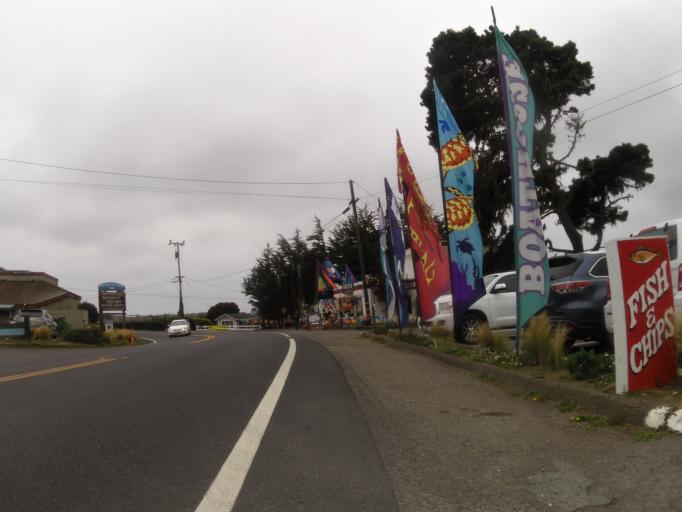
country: US
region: California
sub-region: Sonoma County
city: Bodega Bay
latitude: 38.3355
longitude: -123.0486
